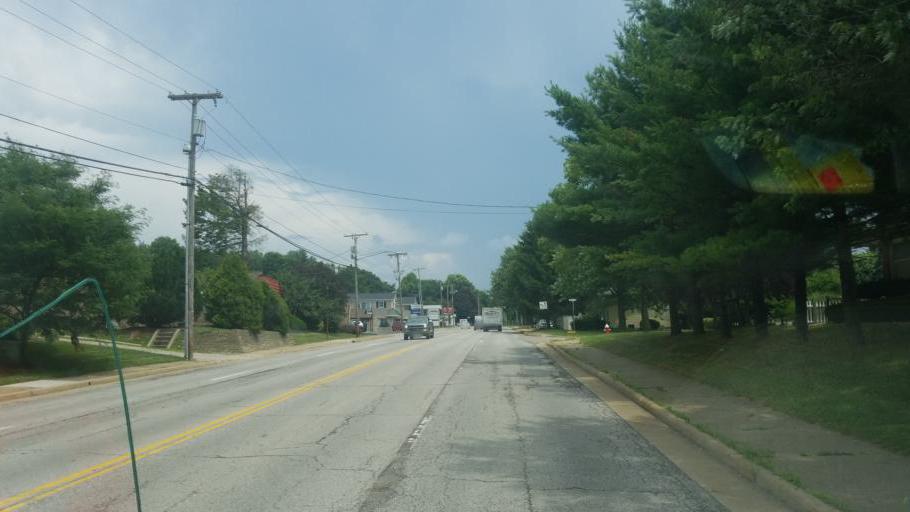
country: US
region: Ohio
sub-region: Stark County
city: North Canton
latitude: 40.8822
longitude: -81.4198
